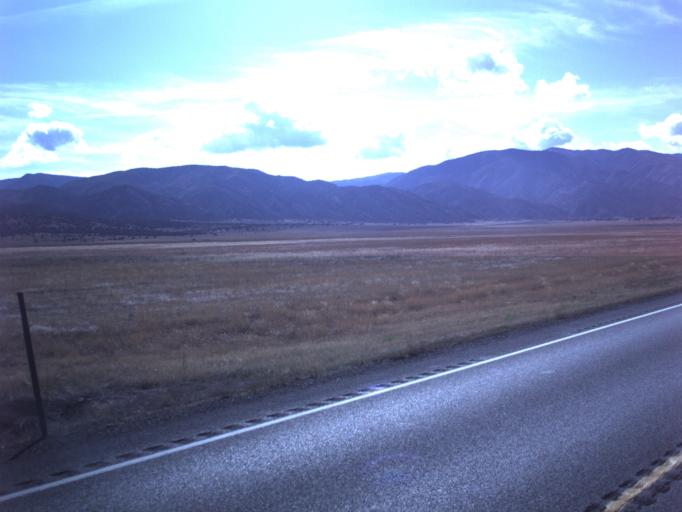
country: US
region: Utah
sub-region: Juab County
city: Nephi
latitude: 39.6070
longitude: -111.8618
